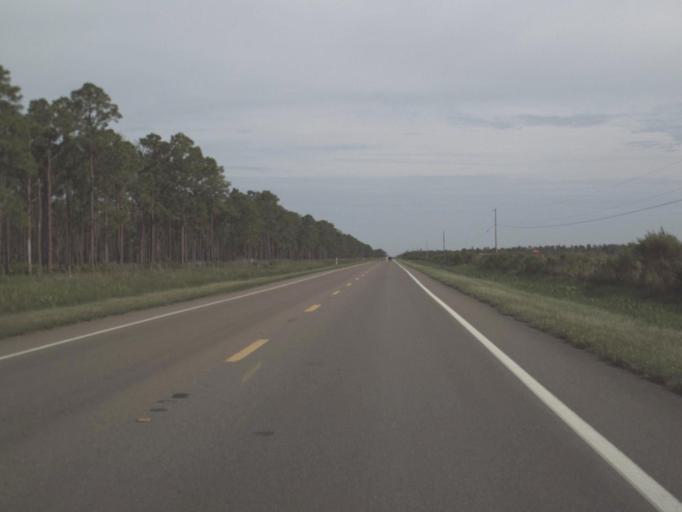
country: US
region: Florida
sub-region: Lee County
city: Olga
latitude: 26.8741
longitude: -81.7599
